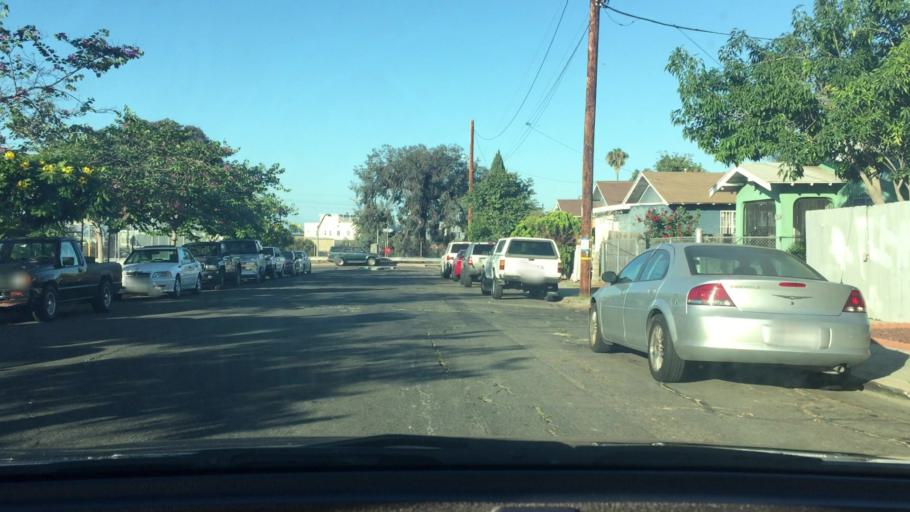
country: US
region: California
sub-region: San Diego County
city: San Diego
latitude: 32.6982
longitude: -117.1364
